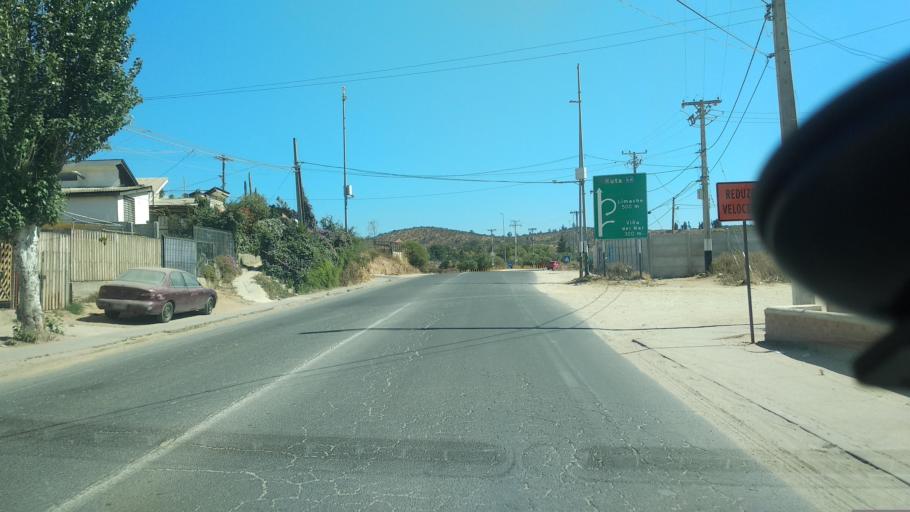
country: CL
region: Valparaiso
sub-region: Provincia de Marga Marga
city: Villa Alemana
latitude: -33.0666
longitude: -71.3712
